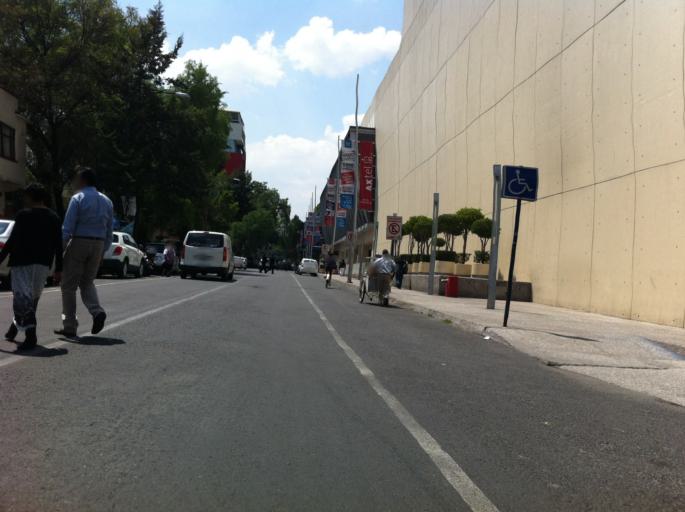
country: MX
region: Mexico City
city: Colonia del Valle
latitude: 19.3929
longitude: -99.1738
